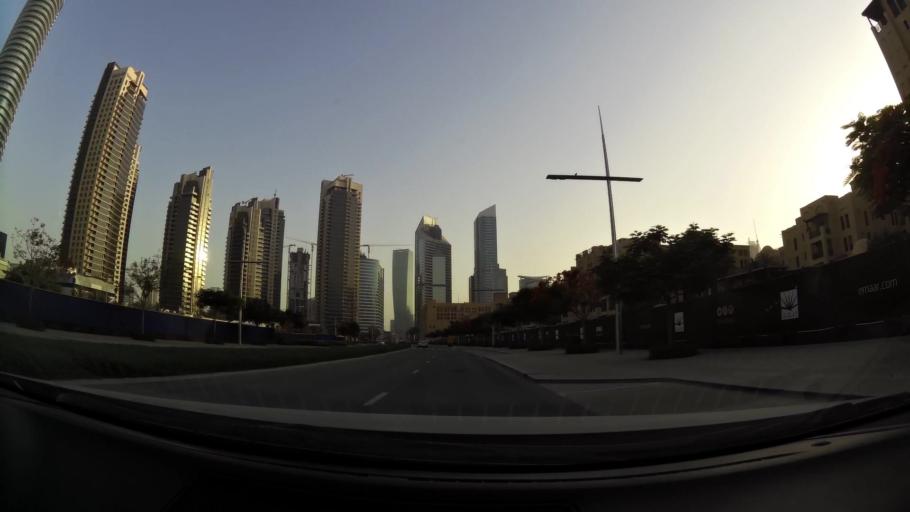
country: AE
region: Dubai
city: Dubai
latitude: 25.1899
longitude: 55.2786
